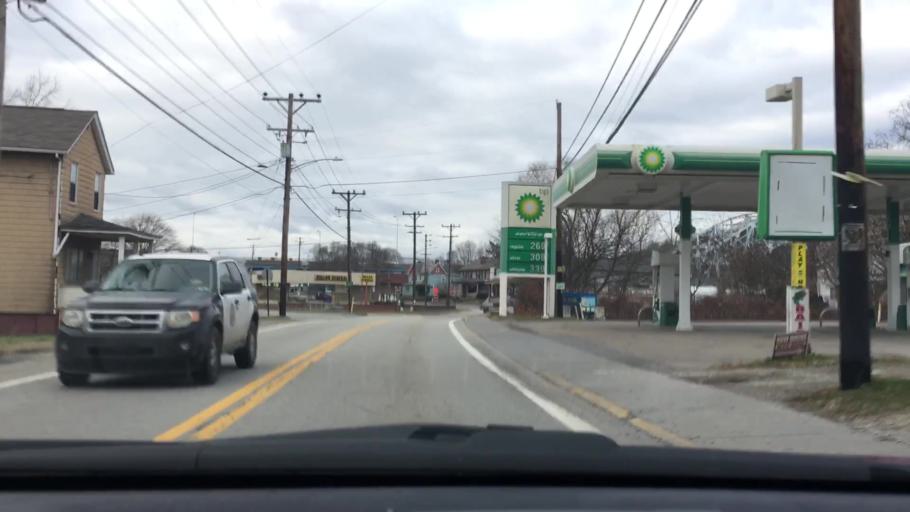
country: US
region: Pennsylvania
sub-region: Allegheny County
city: Elizabeth
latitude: 40.2746
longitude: -79.8832
